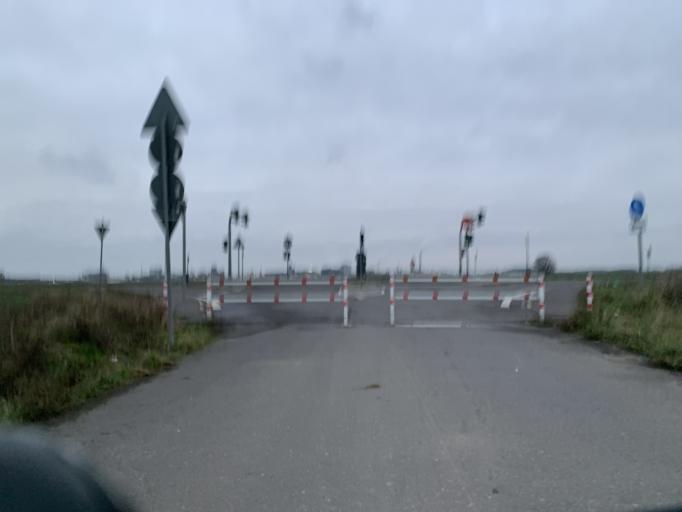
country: DE
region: North Rhine-Westphalia
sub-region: Regierungsbezirk Dusseldorf
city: Krefeld
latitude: 51.3560
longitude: 6.6744
